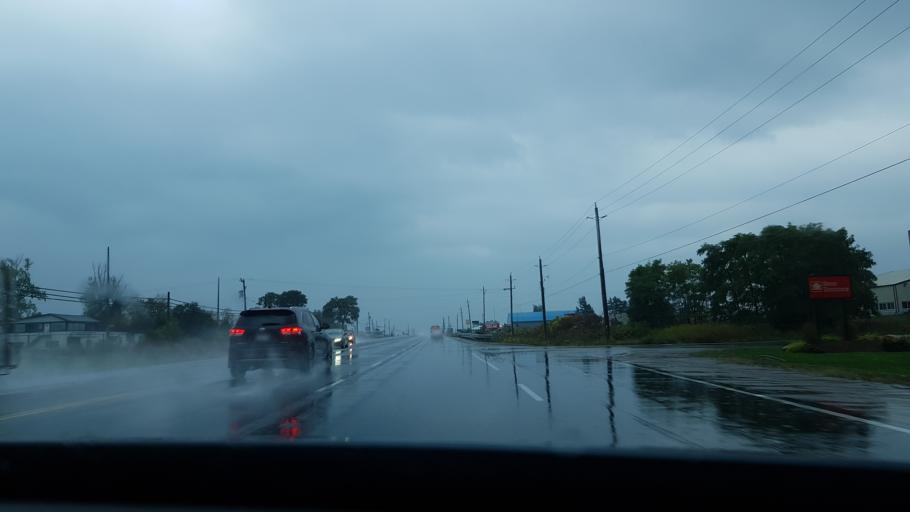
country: CA
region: Ontario
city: Peterborough
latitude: 44.3436
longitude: -78.3562
